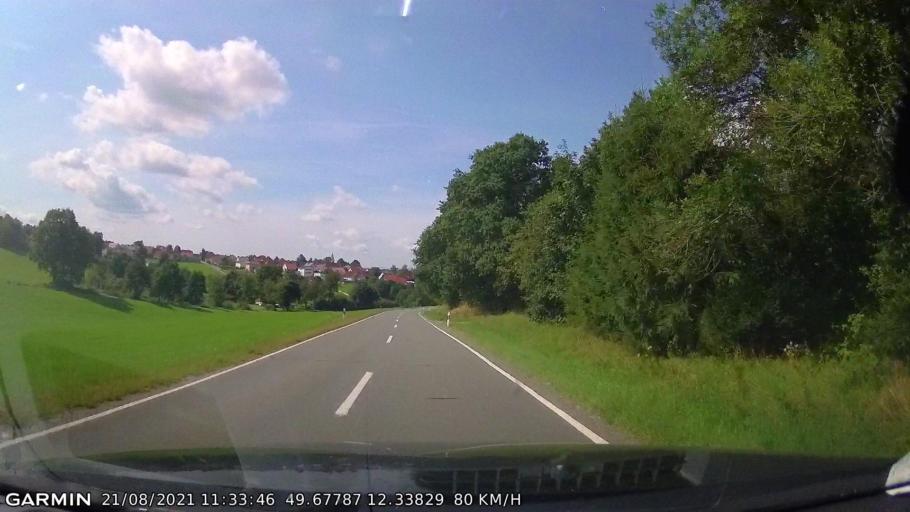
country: DE
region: Bavaria
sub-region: Upper Palatinate
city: Waldthurn
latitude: 49.6778
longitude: 12.3382
